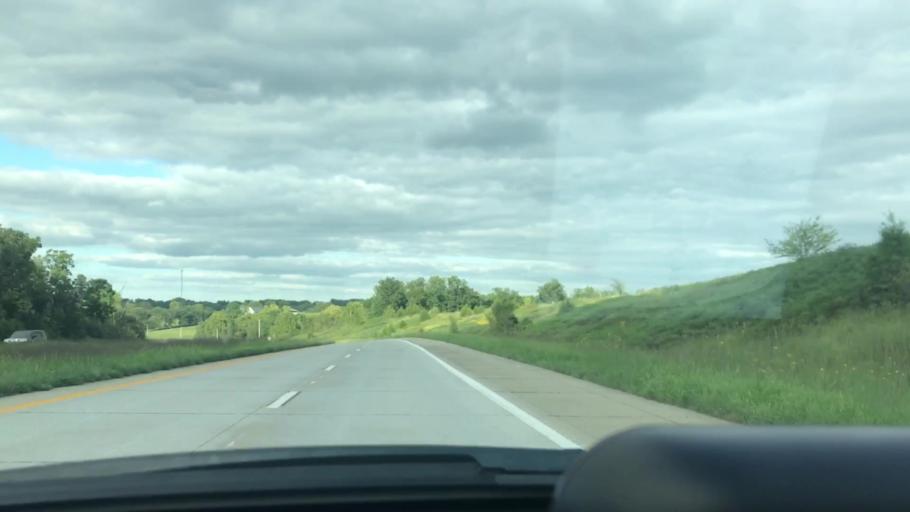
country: US
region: Missouri
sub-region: Benton County
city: Lincoln
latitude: 38.4464
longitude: -93.2905
